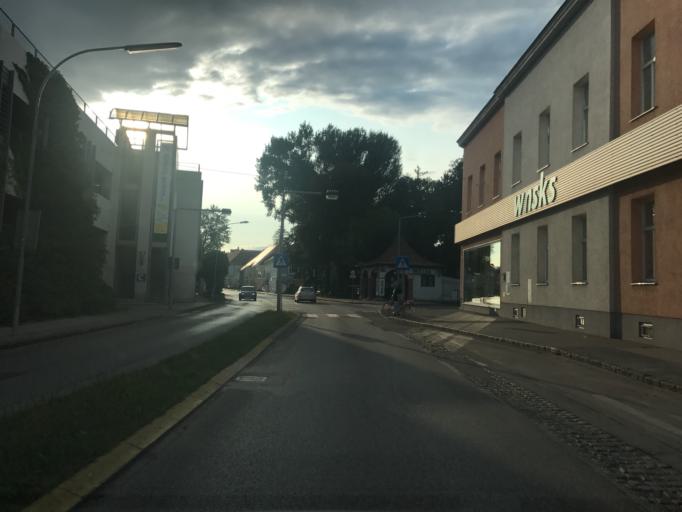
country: AT
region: Lower Austria
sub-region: Wiener Neustadt Stadt
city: Wiener Neustadt
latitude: 47.8126
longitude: 16.2494
